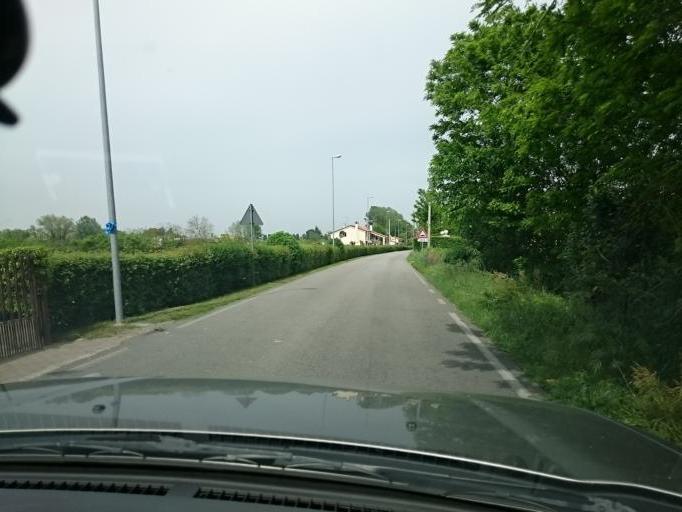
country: IT
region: Veneto
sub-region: Provincia di Venezia
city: Arino
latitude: 45.4148
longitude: 12.0585
